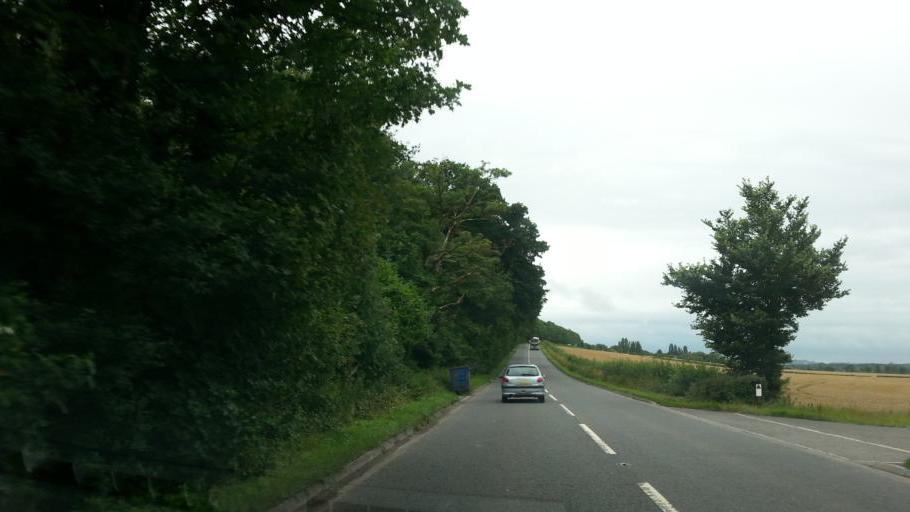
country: GB
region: England
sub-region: Wiltshire
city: North Bradley
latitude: 51.3087
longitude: -2.1722
